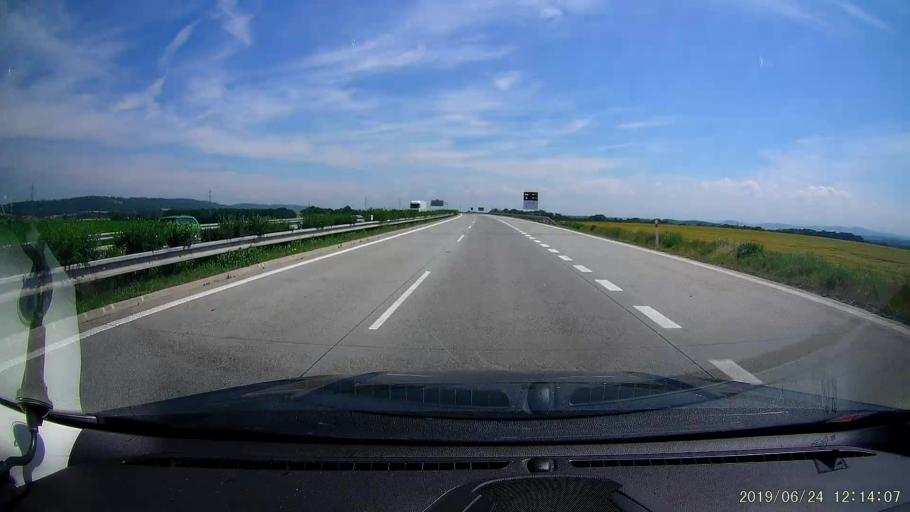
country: CZ
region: Olomoucky
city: Belotin
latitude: 49.5892
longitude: 17.7751
